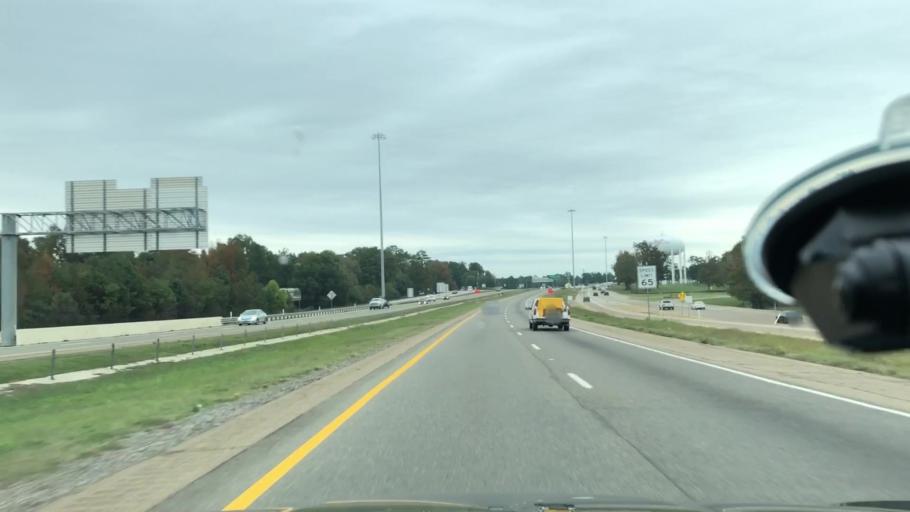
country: US
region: Arkansas
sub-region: Miller County
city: Texarkana
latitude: 33.4678
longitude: -94.0610
